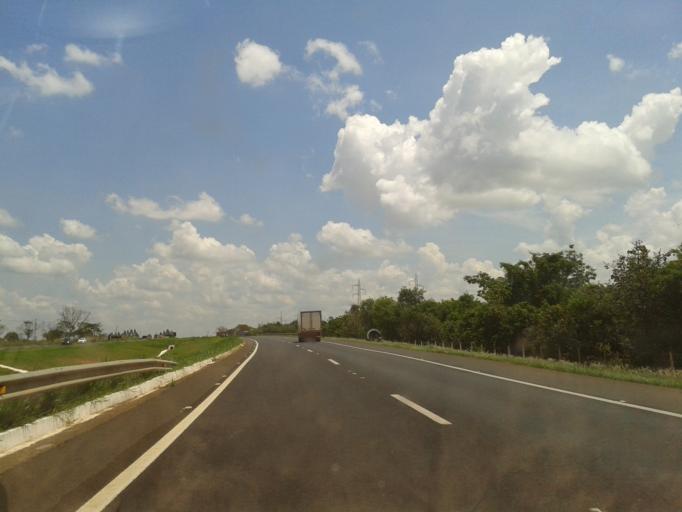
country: BR
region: Minas Gerais
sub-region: Uberlandia
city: Uberlandia
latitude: -18.8750
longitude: -48.5265
